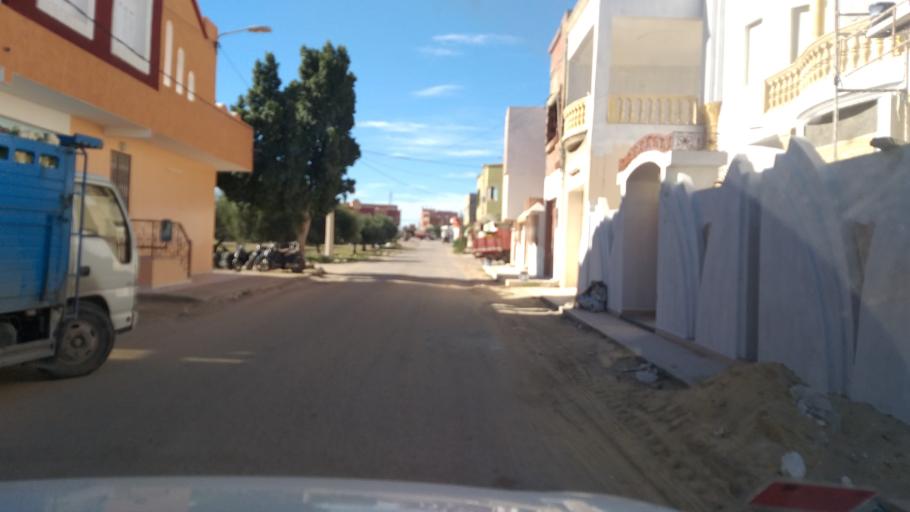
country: TN
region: Al Mahdiyah
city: El Jem
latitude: 35.2933
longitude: 10.6962
